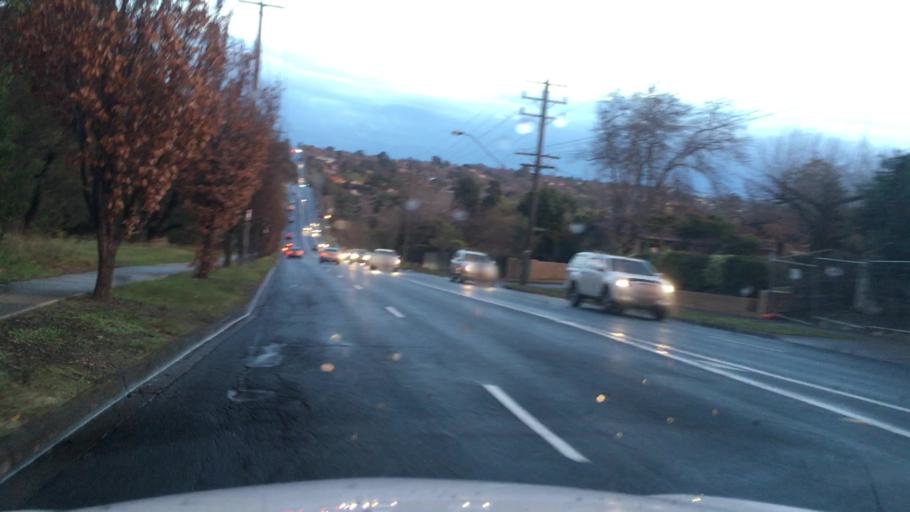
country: AU
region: Victoria
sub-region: Whitehorse
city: Surrey Hills
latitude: -37.8366
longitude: 145.0982
